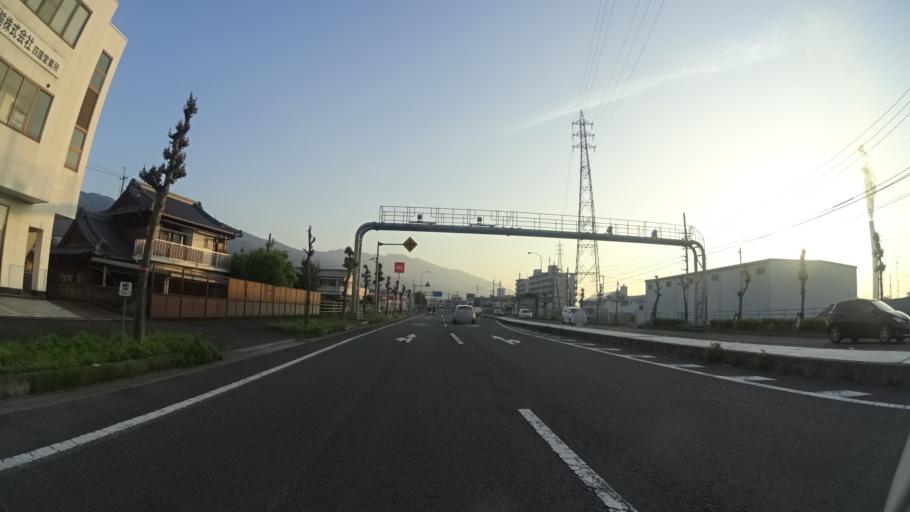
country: JP
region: Ehime
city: Kawanoecho
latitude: 33.9865
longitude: 133.5609
